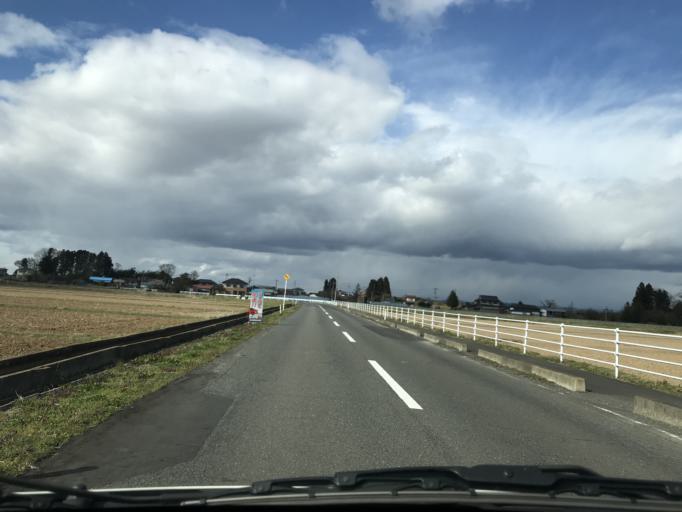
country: JP
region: Miyagi
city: Wakuya
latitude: 38.6539
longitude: 141.2047
